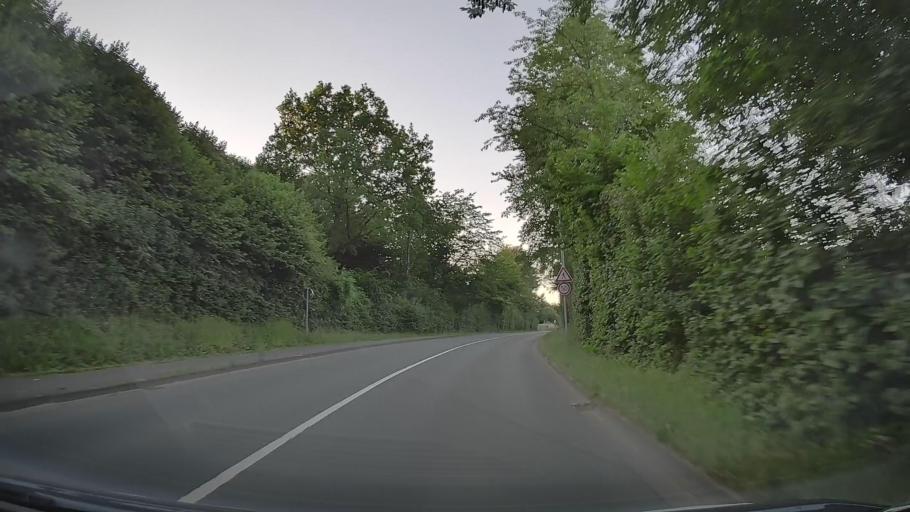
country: DE
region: North Rhine-Westphalia
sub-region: Regierungsbezirk Detmold
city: Lugde
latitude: 51.9599
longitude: 9.2400
